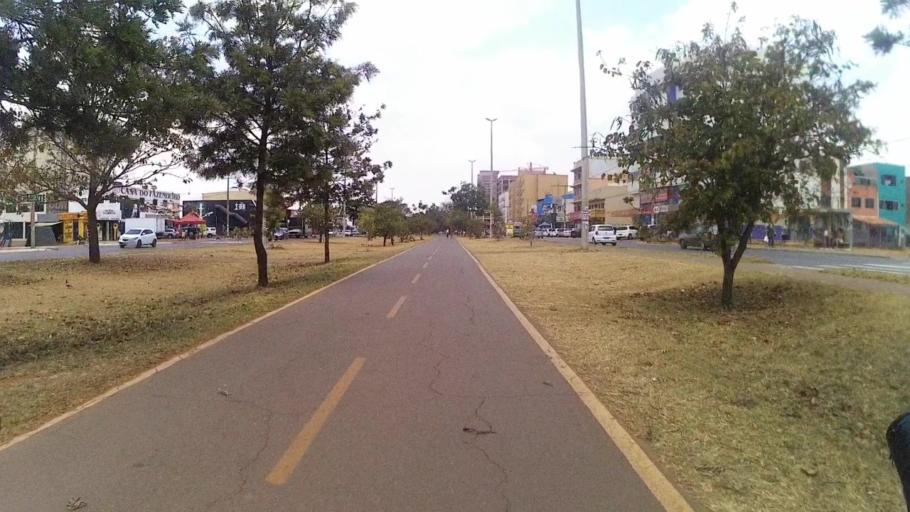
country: BR
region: Federal District
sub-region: Brasilia
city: Brasilia
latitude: -15.8708
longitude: -48.0637
